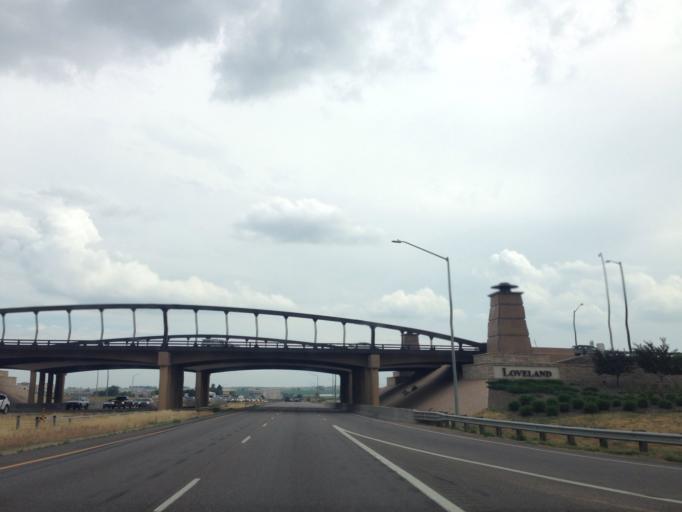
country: US
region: Colorado
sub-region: Larimer County
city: Loveland
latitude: 40.4080
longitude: -104.9933
